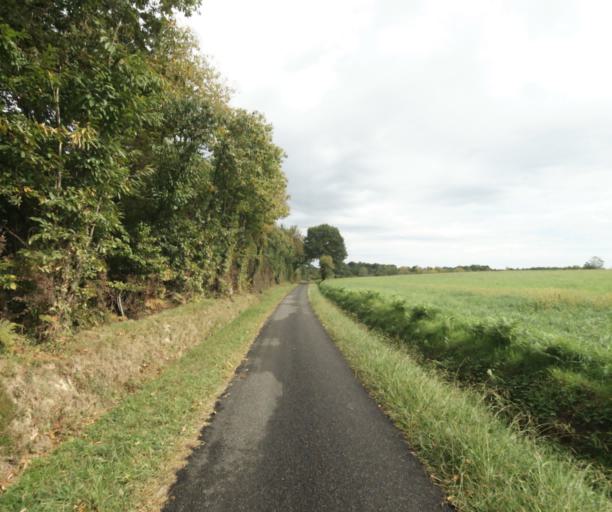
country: FR
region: Midi-Pyrenees
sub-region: Departement du Gers
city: Cazaubon
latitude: 43.8938
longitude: -0.0989
